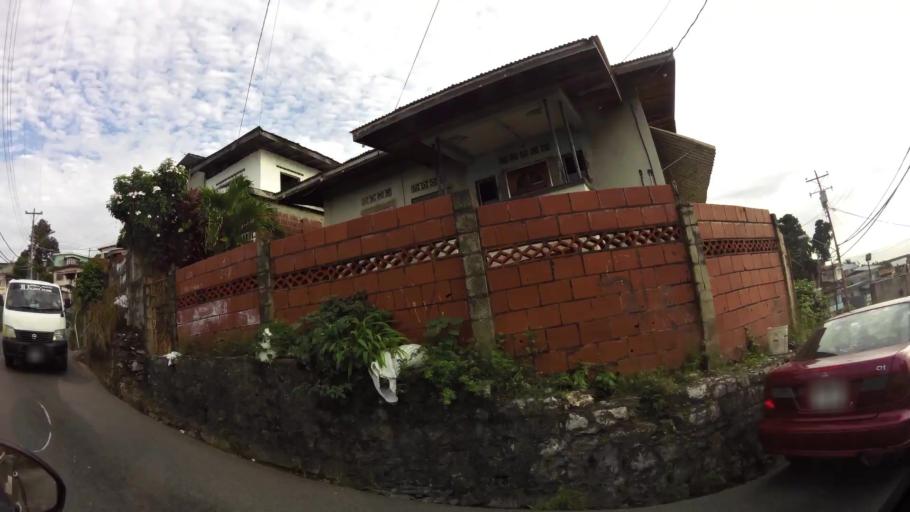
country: TT
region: San Juan/Laventille
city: Laventille
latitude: 10.6570
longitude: -61.4987
